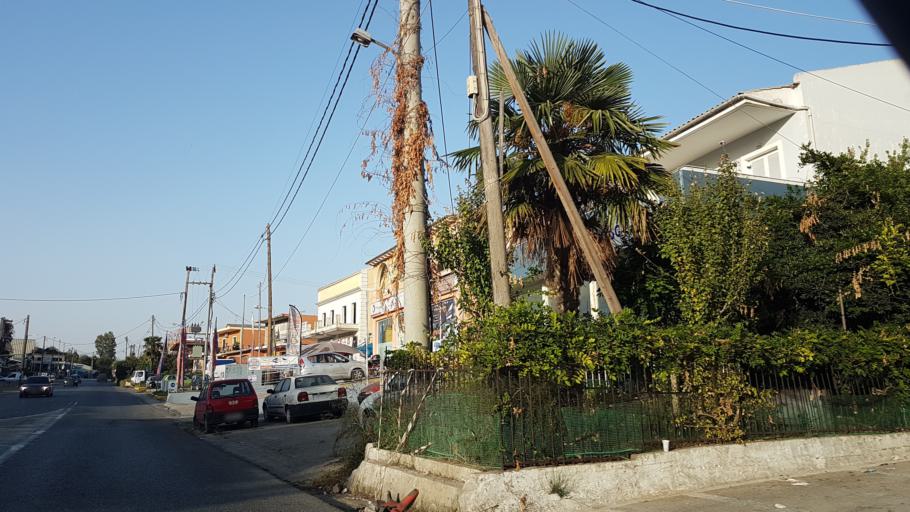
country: GR
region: Ionian Islands
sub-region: Nomos Kerkyras
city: Kanali
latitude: 39.5998
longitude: 19.8939
